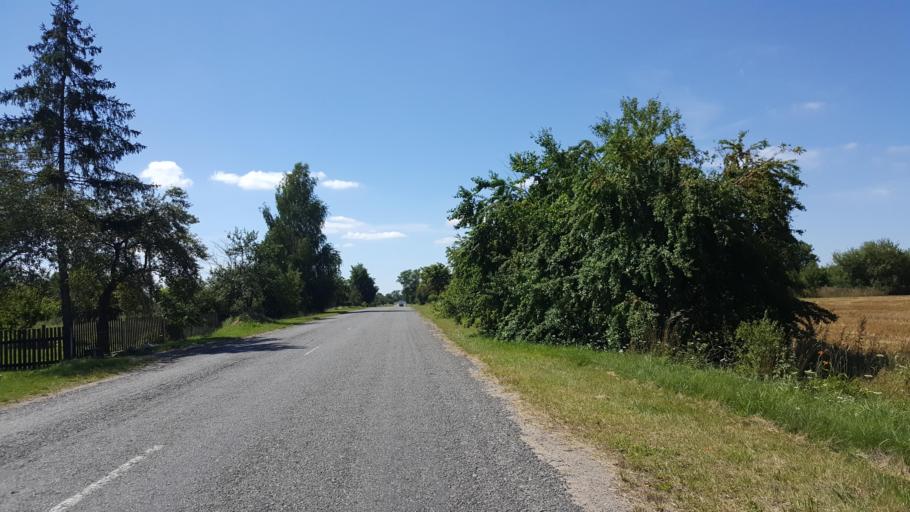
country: BY
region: Brest
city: Kamyanyets
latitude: 52.3742
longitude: 23.6303
